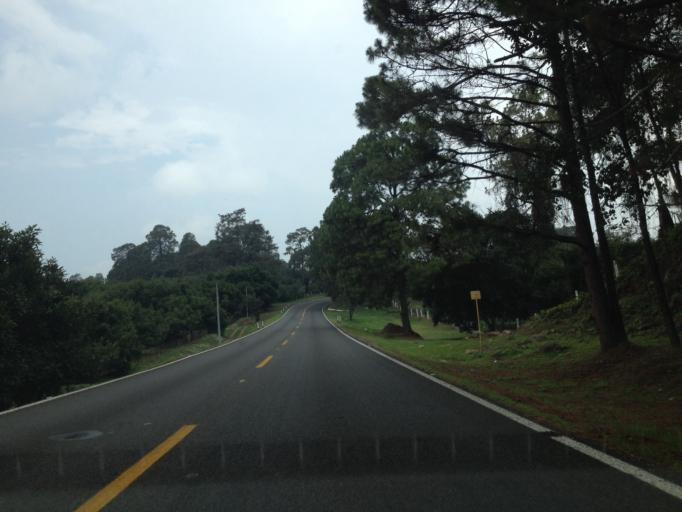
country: MX
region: Michoacan
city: Tingambato
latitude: 19.4768
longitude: -101.9025
